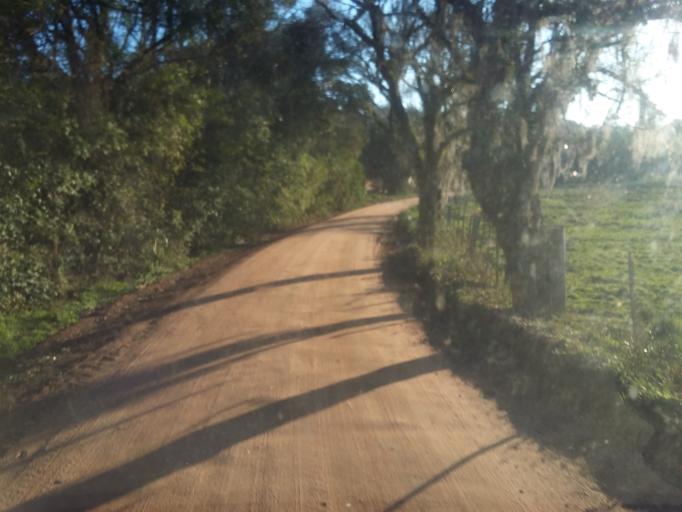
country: BR
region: Rio Grande do Sul
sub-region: Camaqua
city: Camaqua
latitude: -30.7255
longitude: -51.7740
